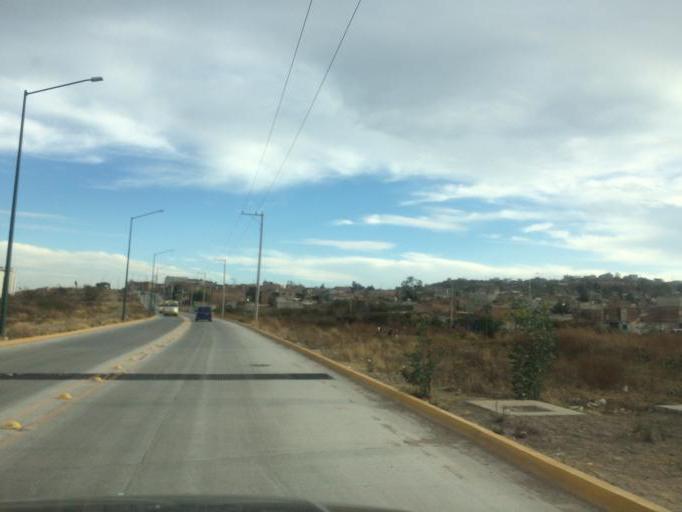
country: MX
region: Guanajuato
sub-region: Leon
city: Rizos de la Joya (Rizos del Saucillo)
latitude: 21.1470
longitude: -101.7552
